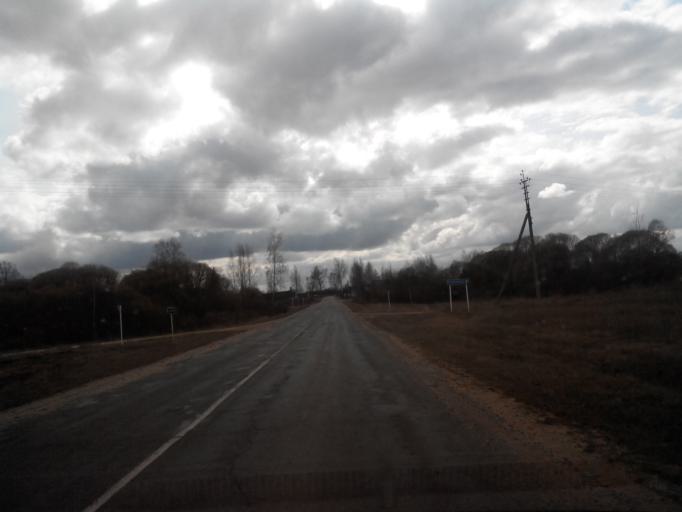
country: BY
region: Vitebsk
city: Pastavy
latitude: 55.1278
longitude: 26.9343
